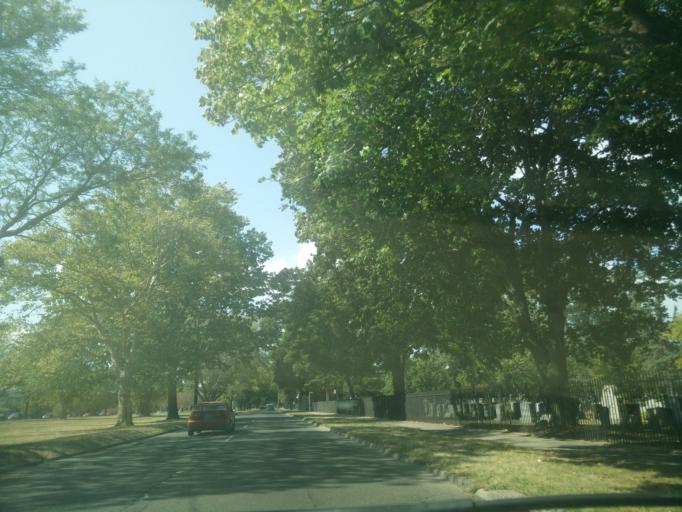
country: US
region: Connecticut
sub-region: Fairfield County
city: Stratford
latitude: 41.1943
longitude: -73.1733
